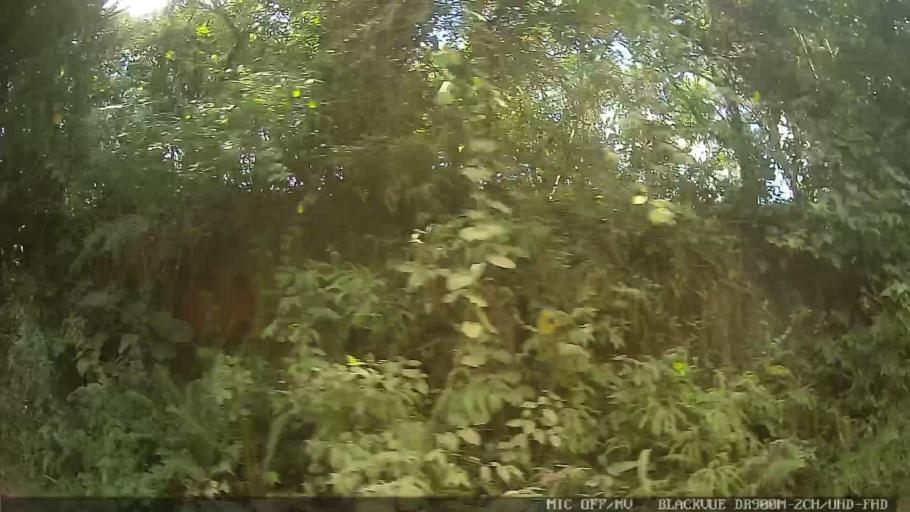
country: BR
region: Sao Paulo
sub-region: Bom Jesus Dos Perdoes
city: Bom Jesus dos Perdoes
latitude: -23.1291
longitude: -46.4998
